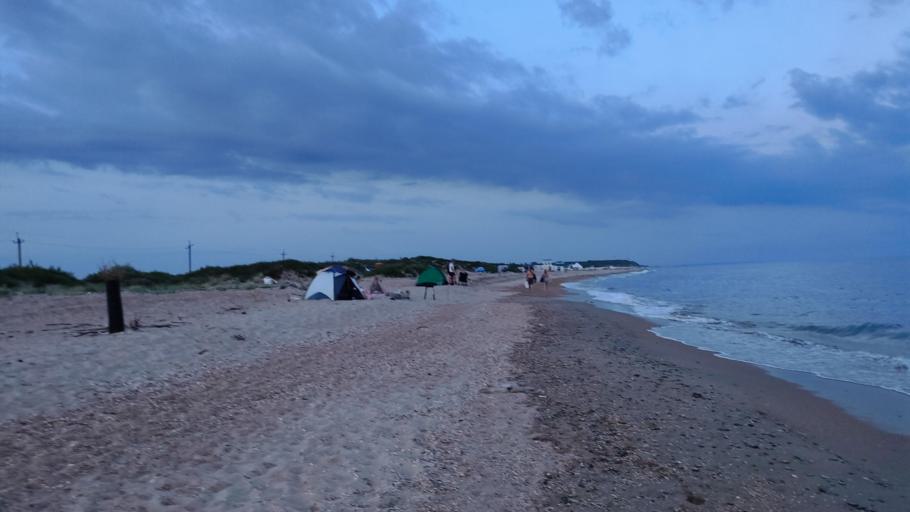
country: RU
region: Krasnodarskiy
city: Blagovetschenskaya
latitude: 45.0674
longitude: 37.0284
